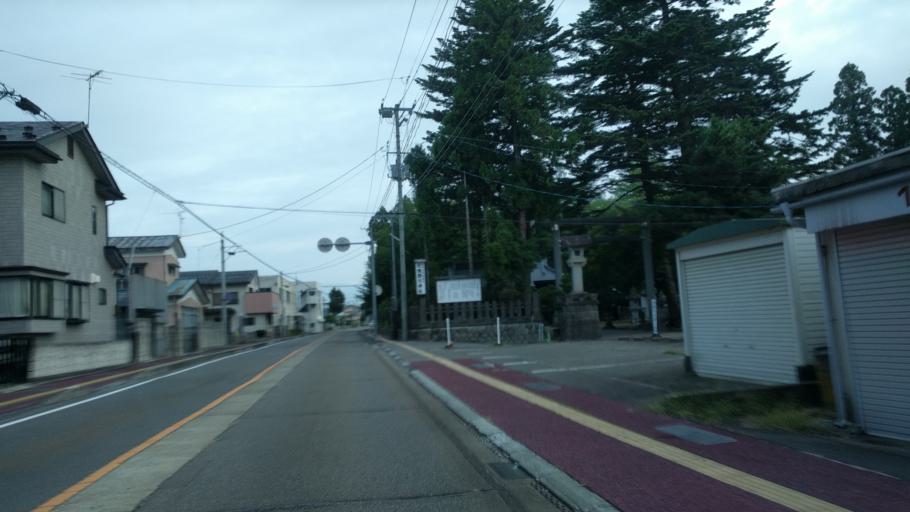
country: JP
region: Fukushima
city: Kitakata
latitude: 37.6530
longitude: 139.8694
